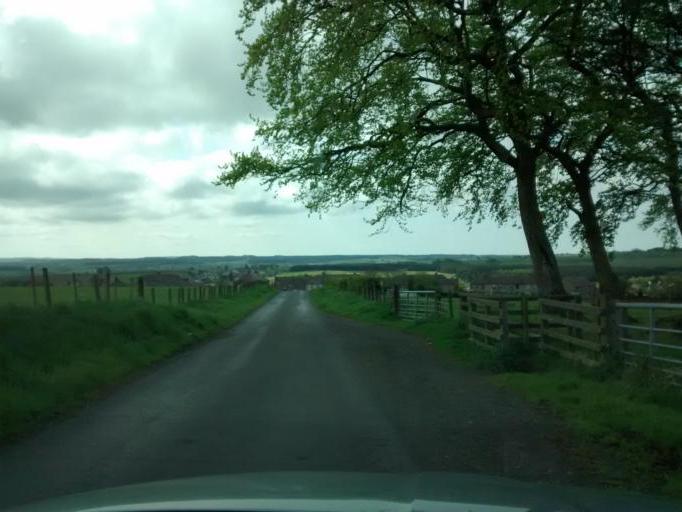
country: GB
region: Scotland
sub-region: North Lanarkshire
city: Harthill
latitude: 55.8875
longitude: -3.7663
